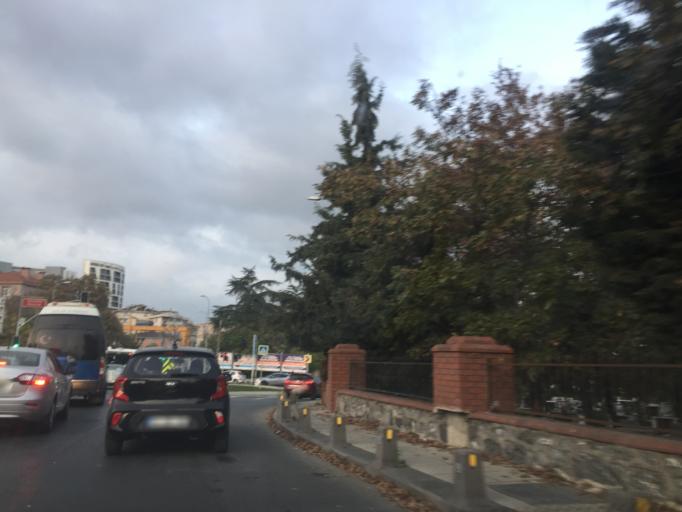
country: TR
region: Istanbul
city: Samandira
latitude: 40.9832
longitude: 29.2315
